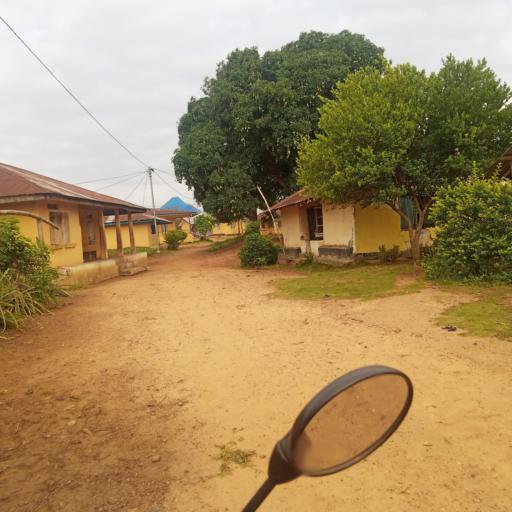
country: SL
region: Eastern Province
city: Pendembu
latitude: 8.0999
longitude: -10.6931
